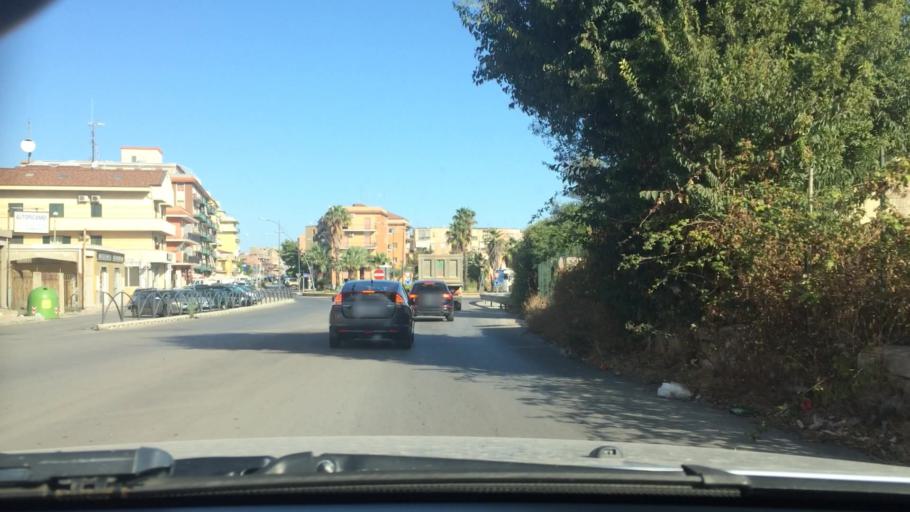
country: IT
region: Sicily
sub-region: Provincia di Siracusa
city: Priolo Gargallo
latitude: 37.1527
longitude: 15.1914
